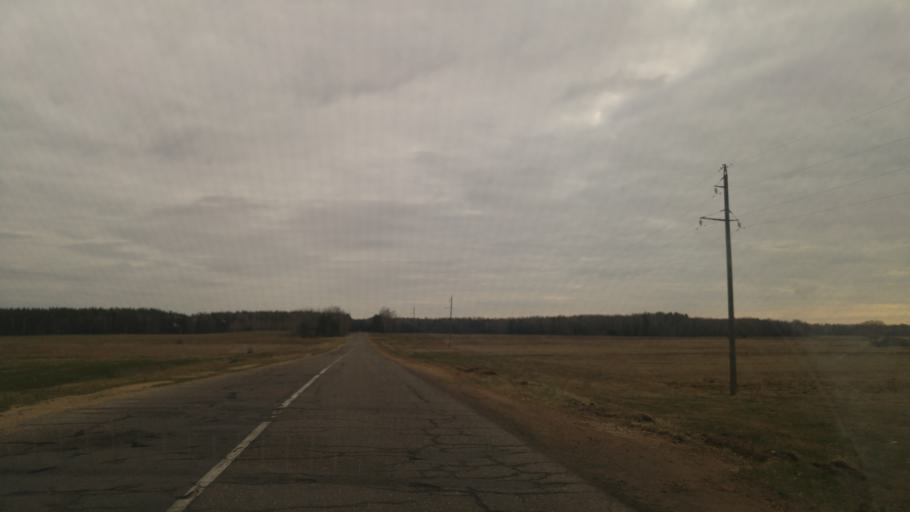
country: BY
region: Minsk
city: Pukhavichy
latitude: 53.7032
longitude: 28.2325
